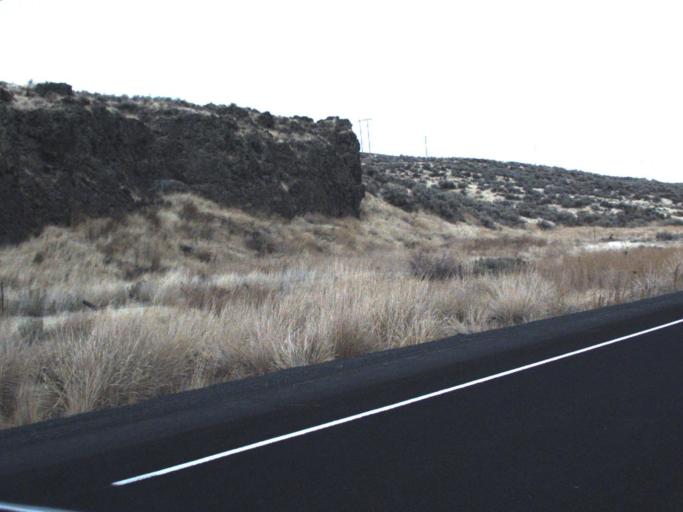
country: US
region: Washington
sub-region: Adams County
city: Ritzville
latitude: 47.3601
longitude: -118.4866
